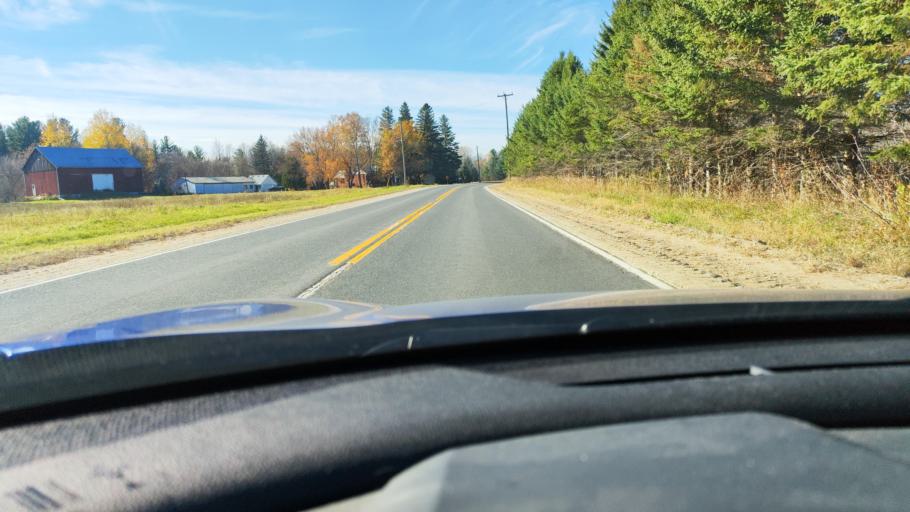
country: CA
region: Ontario
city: Angus
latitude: 44.3443
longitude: -80.0160
